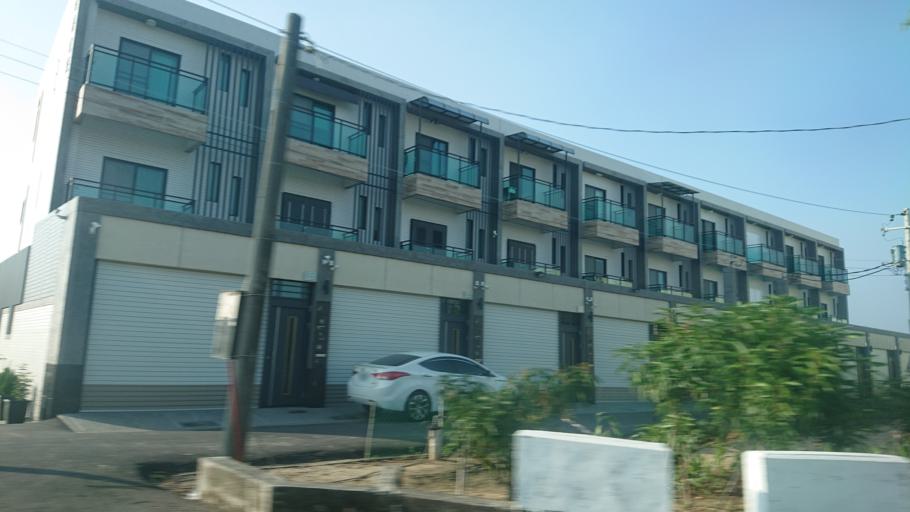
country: TW
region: Taiwan
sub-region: Tainan
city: Tainan
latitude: 23.1307
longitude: 120.2325
